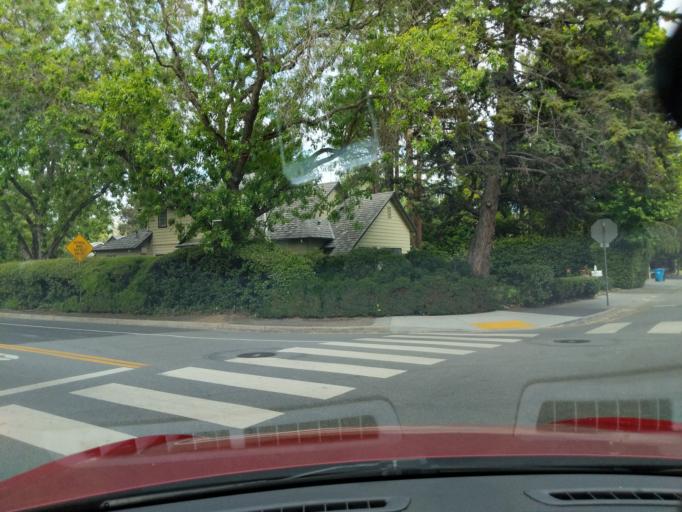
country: US
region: California
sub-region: San Mateo County
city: West Menlo Park
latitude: 37.4374
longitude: -122.1882
